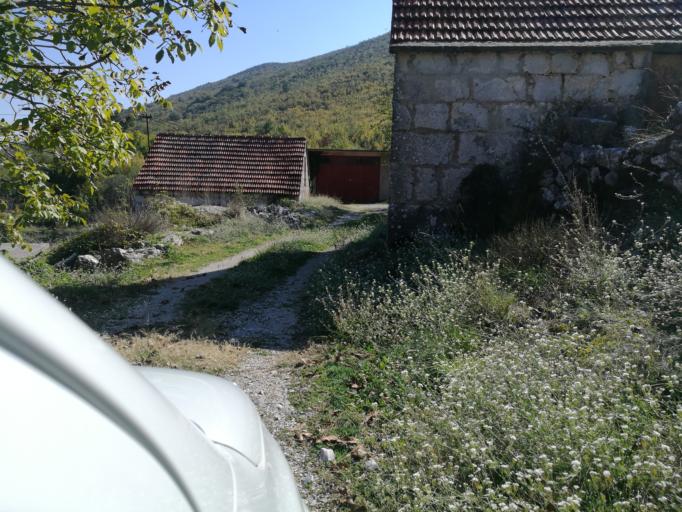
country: HR
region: Splitsko-Dalmatinska
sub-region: Grad Omis
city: Omis
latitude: 43.5127
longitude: 16.7334
